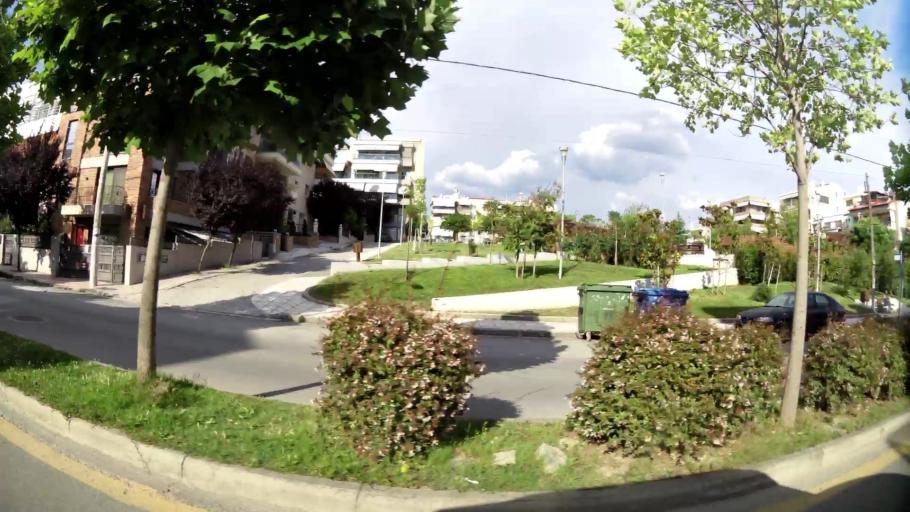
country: GR
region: Central Macedonia
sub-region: Nomos Thessalonikis
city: Kalamaria
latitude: 40.5732
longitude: 22.9657
